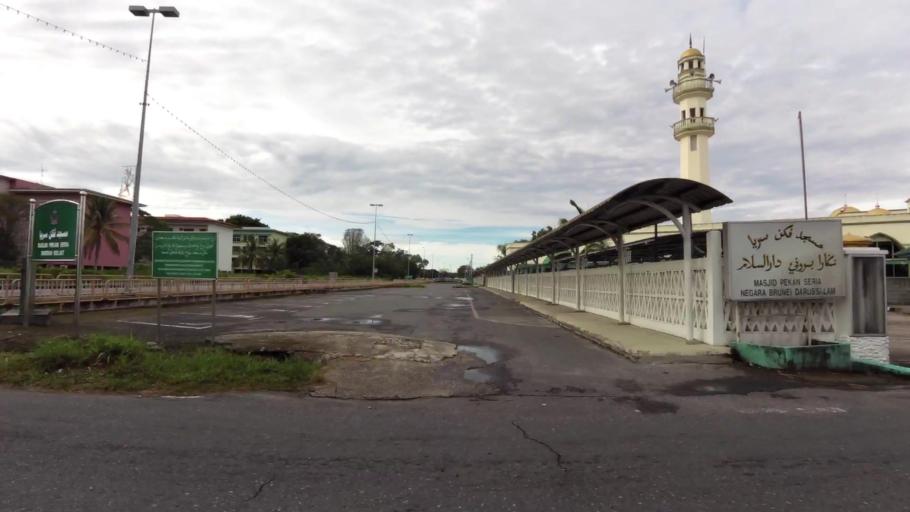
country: BN
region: Belait
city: Seria
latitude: 4.6160
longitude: 114.3336
